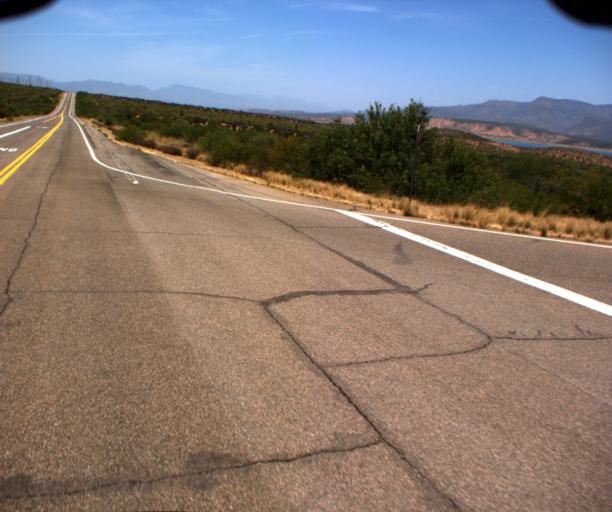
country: US
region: Arizona
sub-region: Gila County
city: Tonto Basin
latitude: 33.6482
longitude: -111.0954
